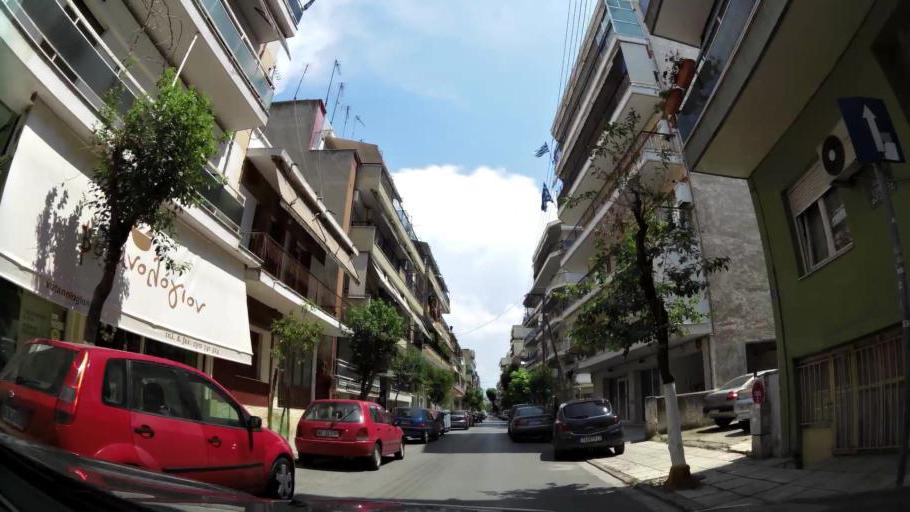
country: GR
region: Central Macedonia
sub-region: Nomos Thessalonikis
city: Ampelokipoi
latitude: 40.6541
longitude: 22.9262
